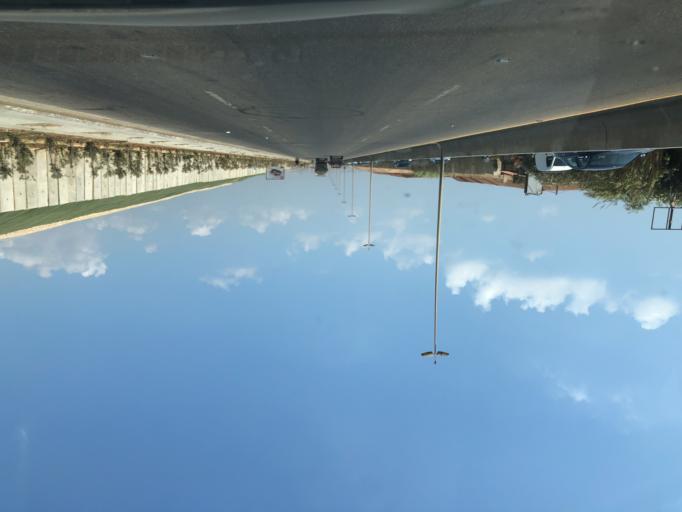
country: LB
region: Mont-Liban
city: Baabda
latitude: 33.8092
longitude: 35.4820
